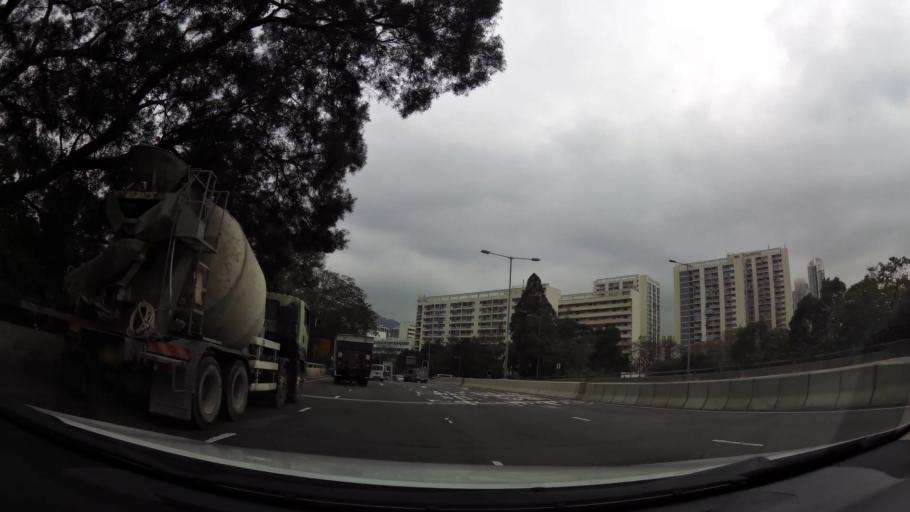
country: HK
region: Sha Tin
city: Sha Tin
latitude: 22.3916
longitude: 114.1970
